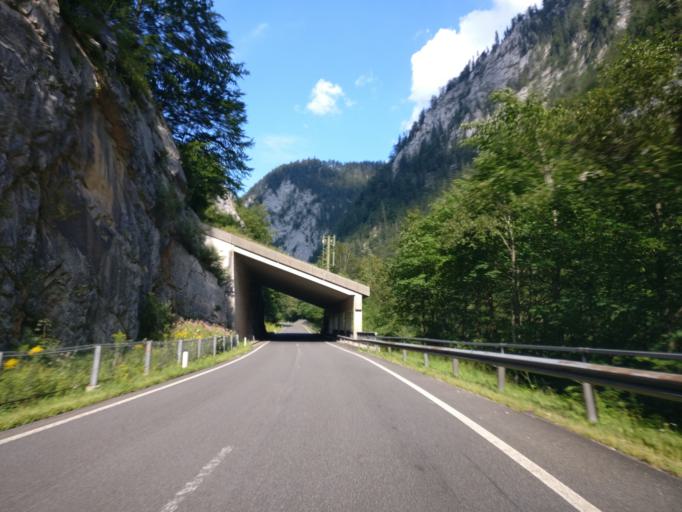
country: AT
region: Styria
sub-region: Politischer Bezirk Leoben
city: Hieflau
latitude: 47.5949
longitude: 14.7144
